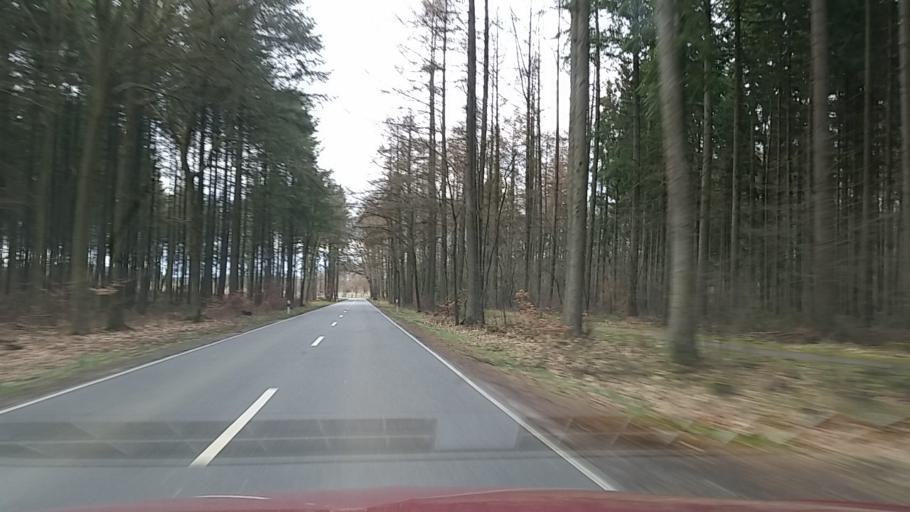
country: DE
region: Lower Saxony
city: Zernien
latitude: 53.1090
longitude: 10.9462
